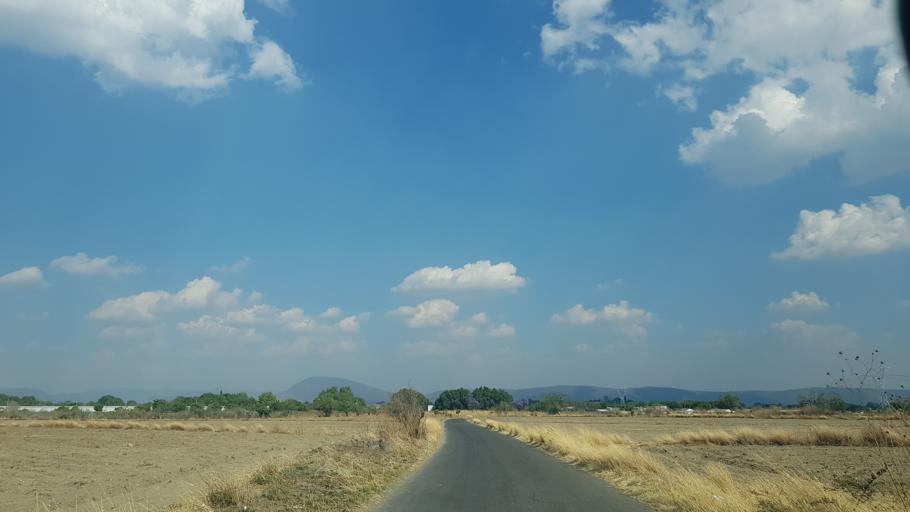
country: MX
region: Puebla
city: Atlixco
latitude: 18.8848
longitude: -98.4942
